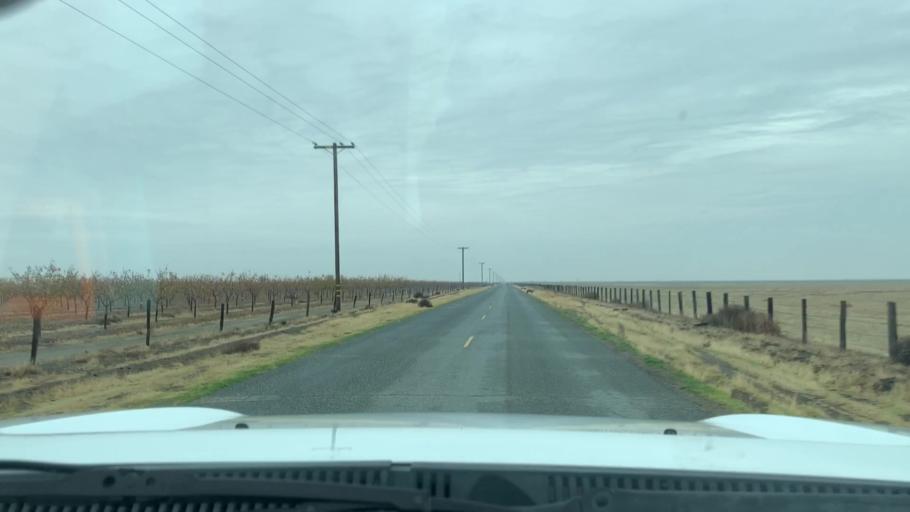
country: US
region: California
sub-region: Tulare County
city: Alpaugh
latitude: 35.7608
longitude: -119.5606
